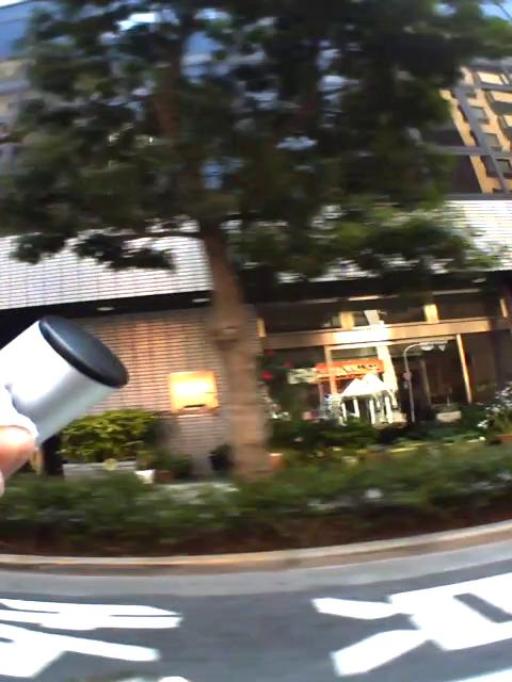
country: JP
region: Osaka
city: Osaka-shi
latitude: 34.6869
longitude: 135.5116
